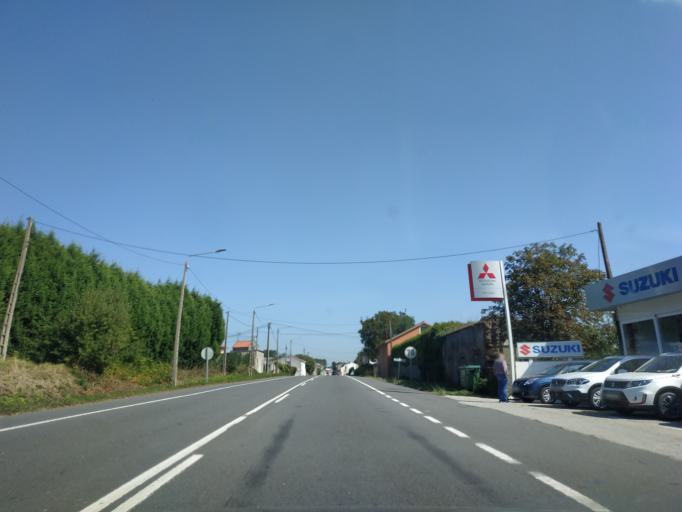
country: ES
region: Galicia
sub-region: Provincia da Coruna
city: Carballo
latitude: 43.2297
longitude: -8.6707
